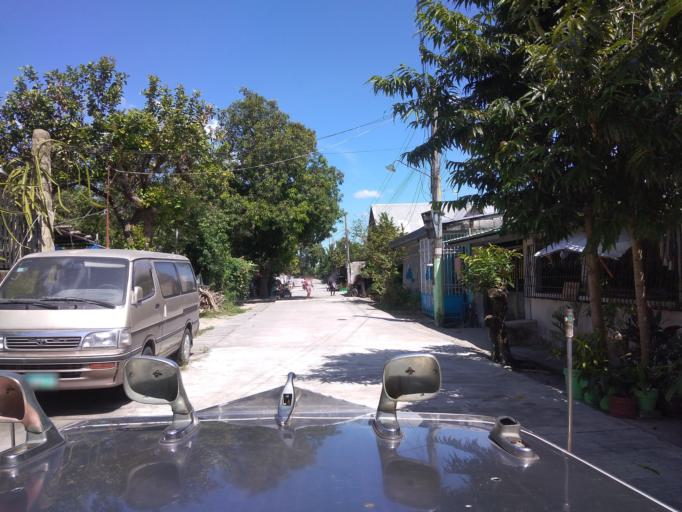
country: PH
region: Central Luzon
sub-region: Province of Pampanga
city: Calibutbut
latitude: 15.0973
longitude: 120.6079
